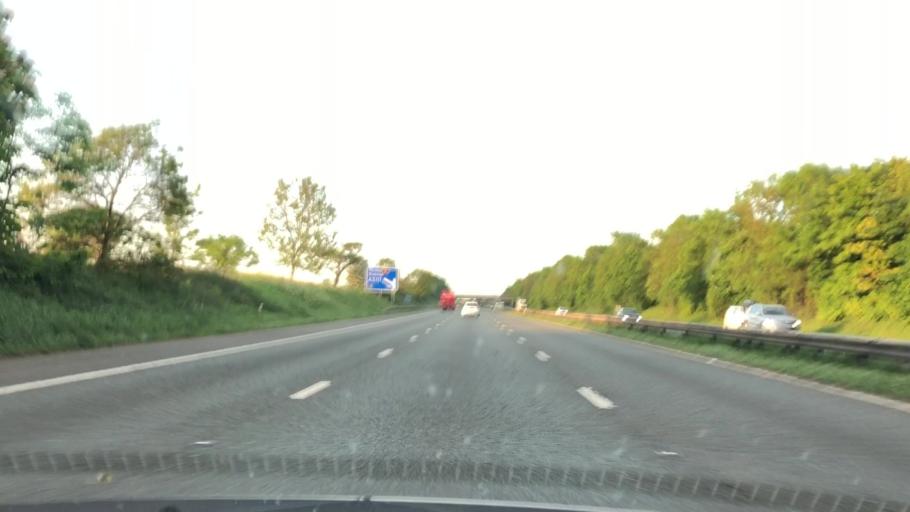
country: GB
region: England
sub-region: Cheshire West and Chester
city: Elton
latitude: 53.2557
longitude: -2.8311
